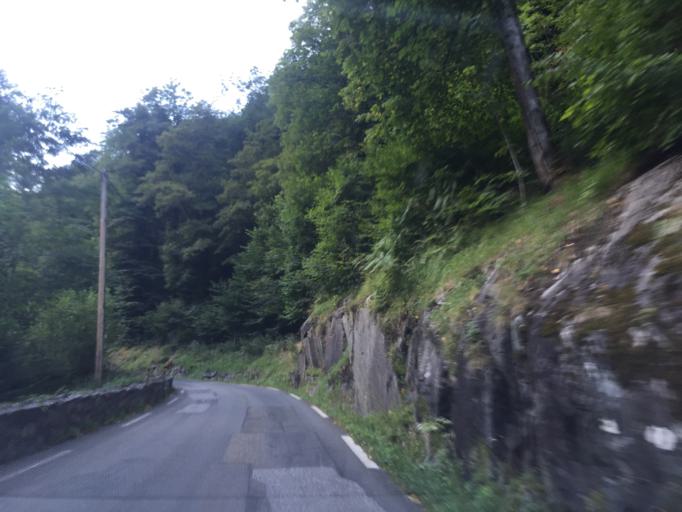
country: FR
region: Midi-Pyrenees
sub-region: Departement des Hautes-Pyrenees
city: Cauterets
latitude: 42.8801
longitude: -0.1122
